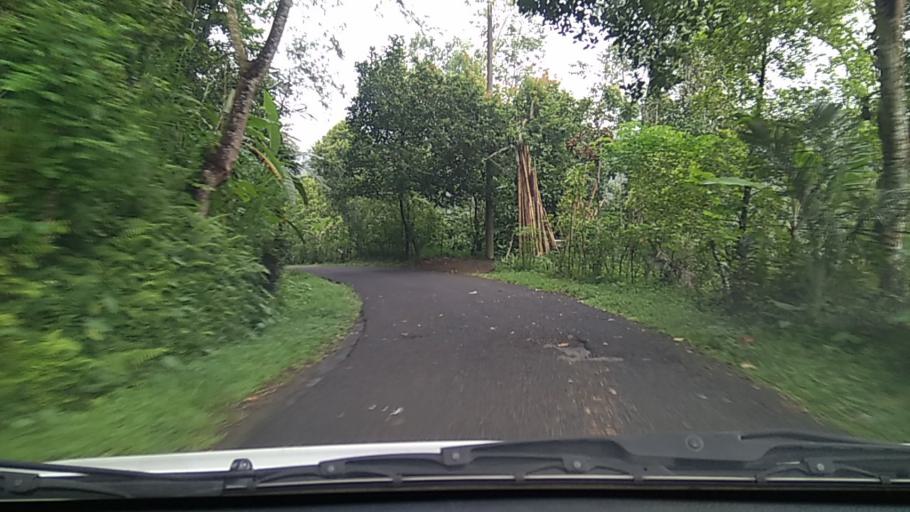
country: ID
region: Bali
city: Banjar Padangbulia
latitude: -8.1845
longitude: 115.1882
